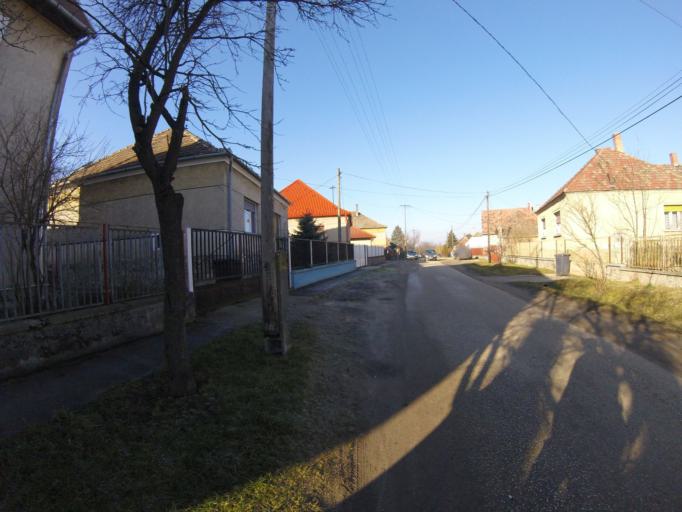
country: HU
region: Komarom-Esztergom
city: Bokod
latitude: 47.5208
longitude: 18.2190
